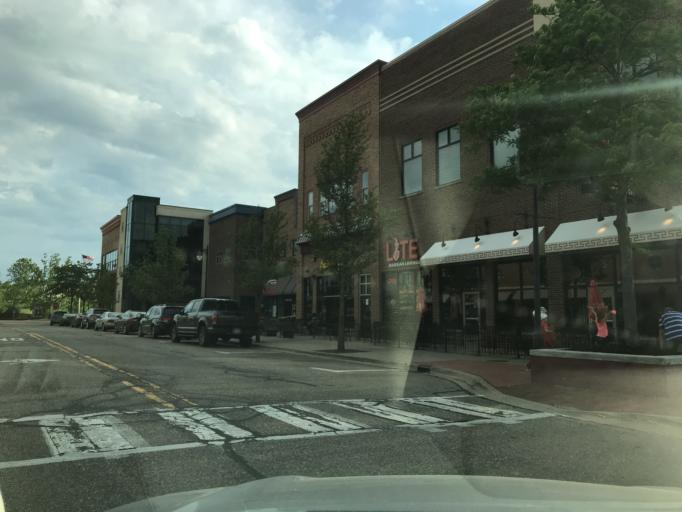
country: US
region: Michigan
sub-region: Oakland County
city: Novi
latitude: 42.4784
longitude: -83.4696
